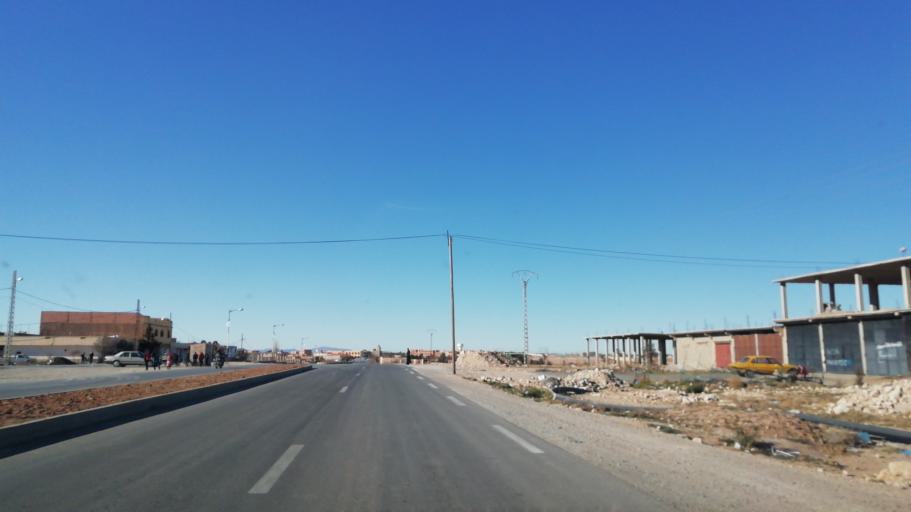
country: DZ
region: Tlemcen
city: Sebdou
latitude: 34.2201
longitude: -1.2493
